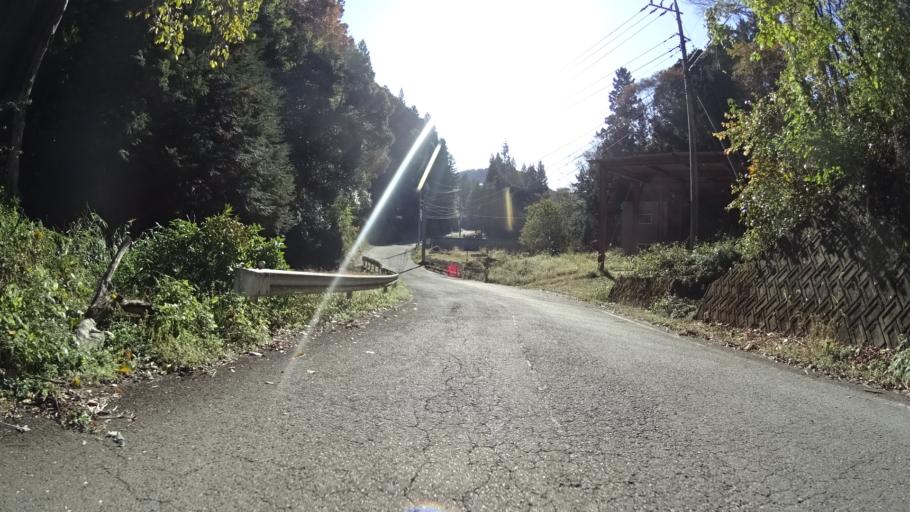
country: JP
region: Yamanashi
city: Uenohara
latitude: 35.6692
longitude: 139.1063
